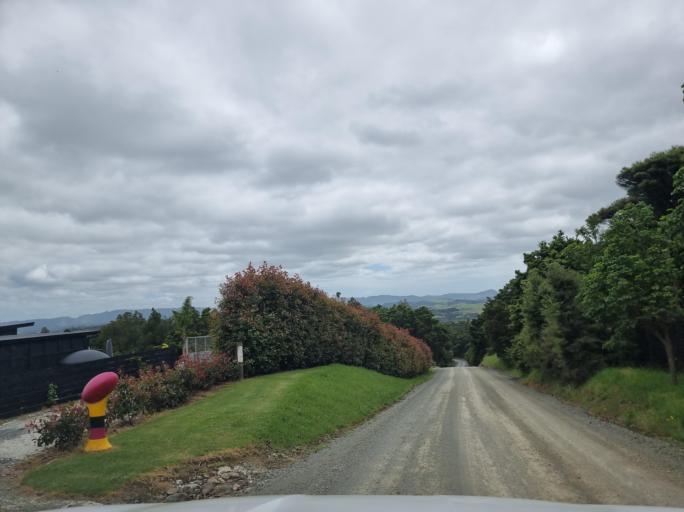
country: NZ
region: Auckland
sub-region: Auckland
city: Wellsford
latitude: -36.1642
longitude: 174.5520
